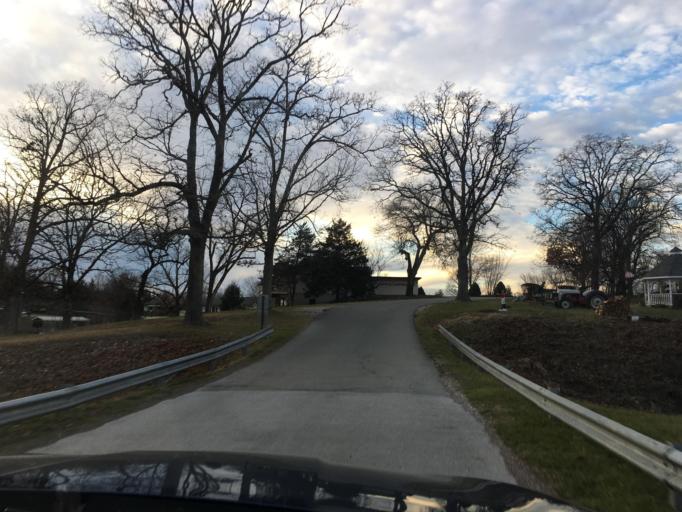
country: US
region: Missouri
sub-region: Jefferson County
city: De Soto
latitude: 38.0967
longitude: -90.5725
